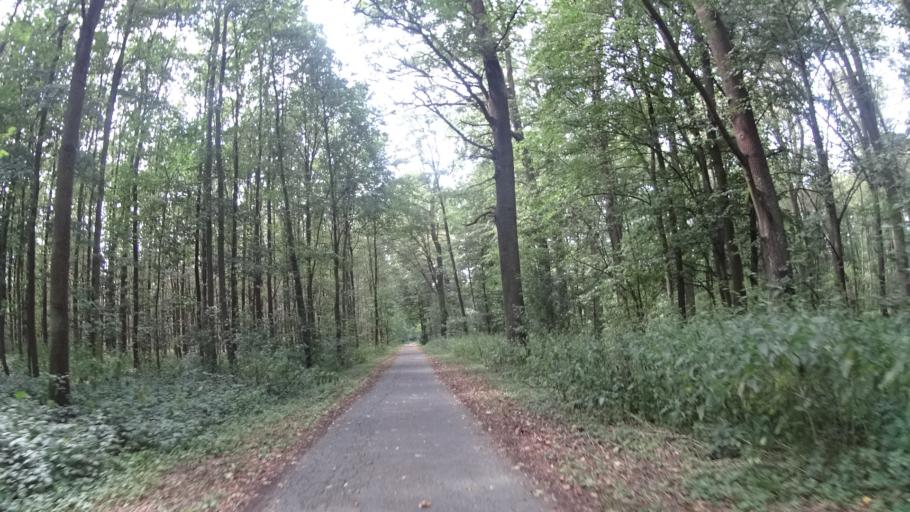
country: CZ
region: Olomoucky
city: Skrben
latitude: 49.6598
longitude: 17.1908
